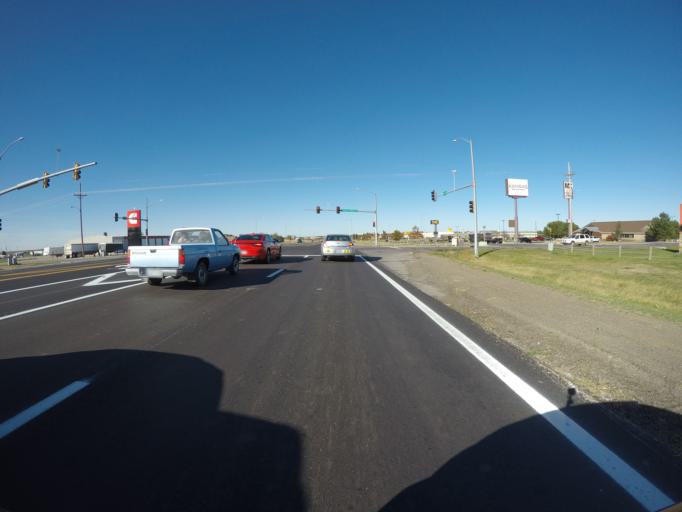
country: US
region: Kansas
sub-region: Thomas County
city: Colby
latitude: 39.3700
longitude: -101.0548
